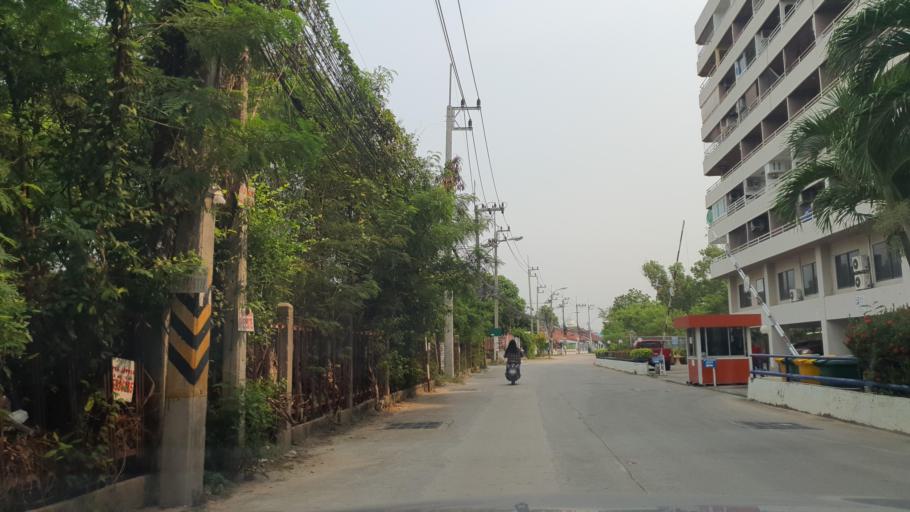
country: TH
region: Chon Buri
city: Phatthaya
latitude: 12.8903
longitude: 100.8845
